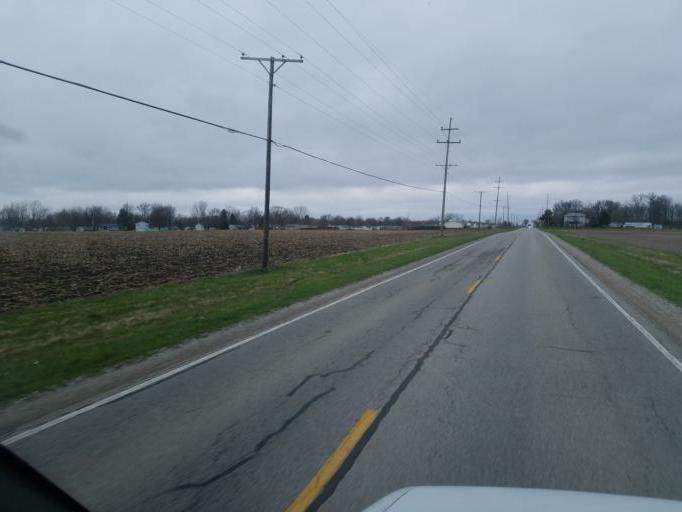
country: US
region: Ohio
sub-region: Marion County
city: Marion
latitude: 40.6332
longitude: -83.0733
